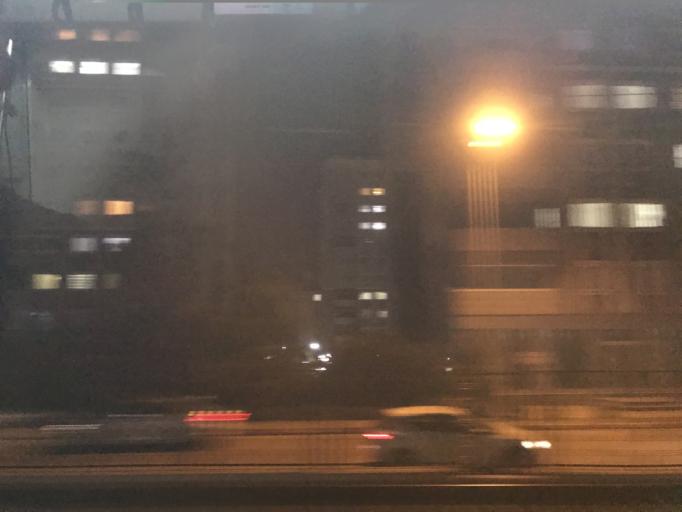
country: TR
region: Istanbul
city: Maltepe
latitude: 40.9000
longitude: 29.1676
